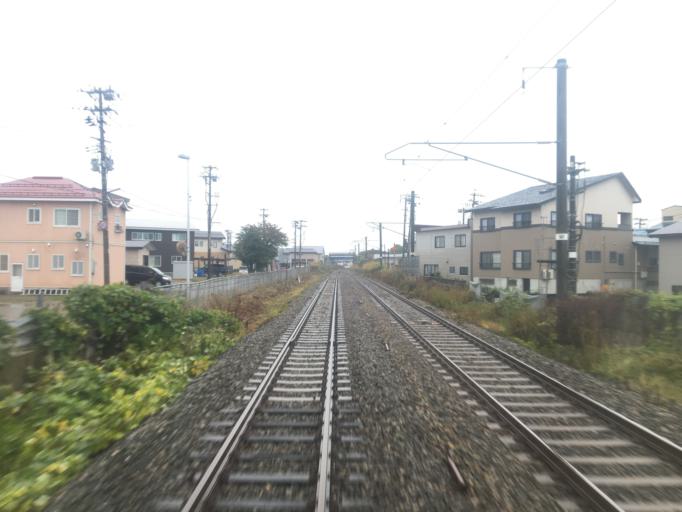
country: JP
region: Yamagata
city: Shinjo
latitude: 38.7497
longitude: 140.3078
